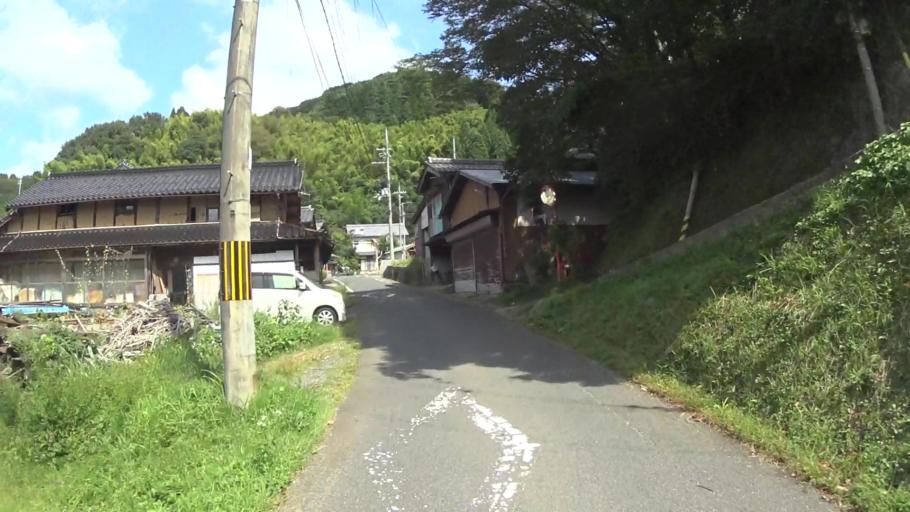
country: JP
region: Kyoto
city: Miyazu
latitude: 35.6722
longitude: 135.2450
